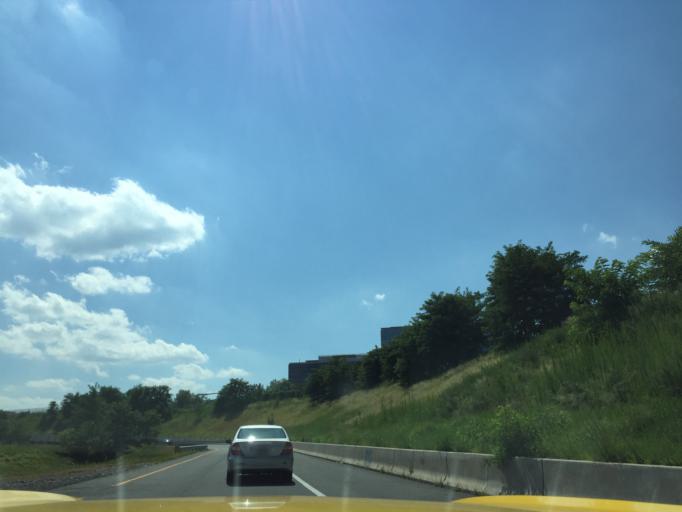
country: US
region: Virginia
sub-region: Fairfax County
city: Tysons Corner
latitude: 38.9237
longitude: -77.2165
